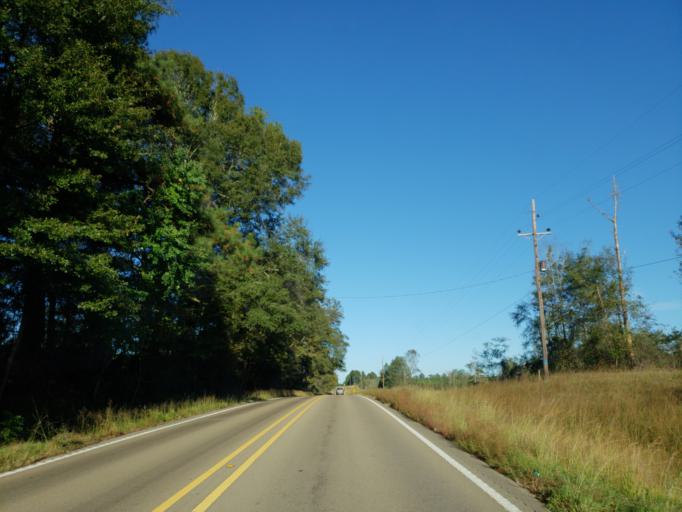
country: US
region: Mississippi
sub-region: Perry County
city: Richton
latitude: 31.3618
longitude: -88.8950
